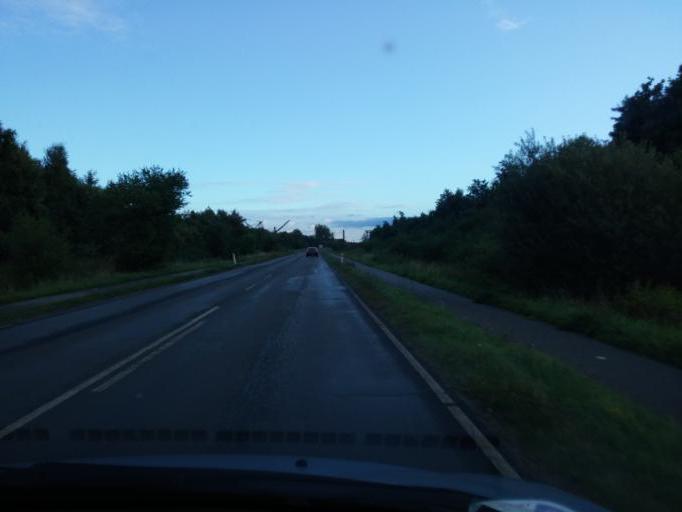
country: DK
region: South Denmark
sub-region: Kerteminde Kommune
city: Munkebo
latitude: 55.4621
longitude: 10.5353
